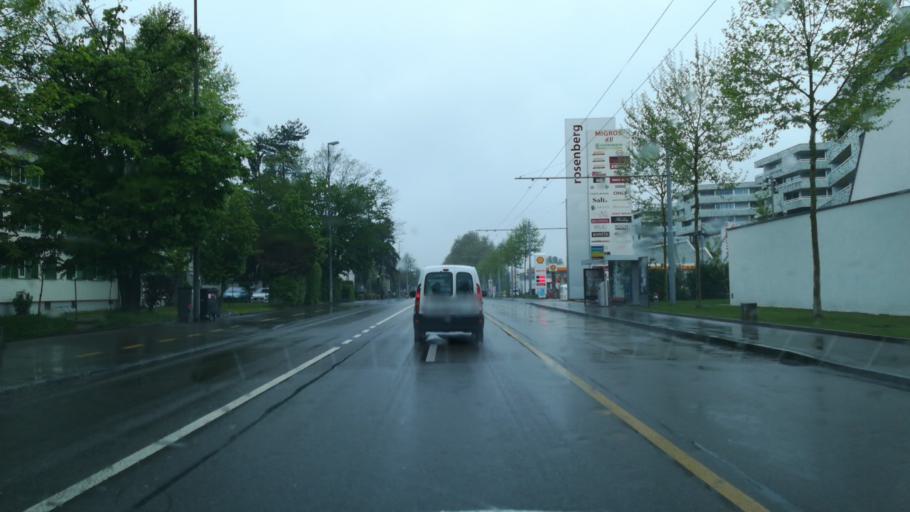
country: CH
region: Zurich
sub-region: Bezirk Winterthur
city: Veltheim
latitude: 47.5173
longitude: 8.7197
